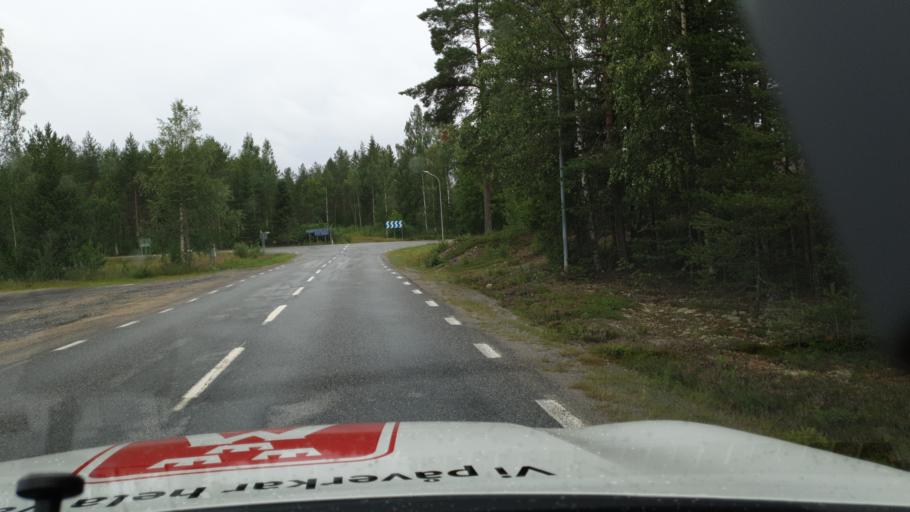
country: SE
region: Vaesterbotten
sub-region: Umea Kommun
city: Saevar
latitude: 64.0255
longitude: 20.4803
